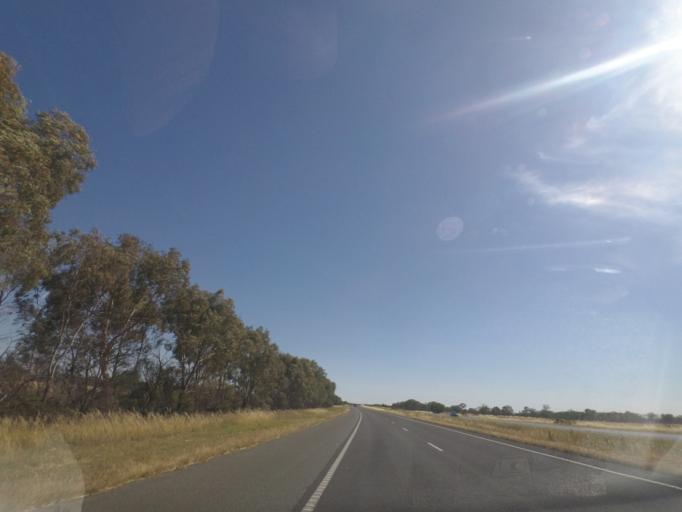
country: AU
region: Victoria
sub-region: Greater Shepparton
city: Shepparton
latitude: -36.6232
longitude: 145.3021
